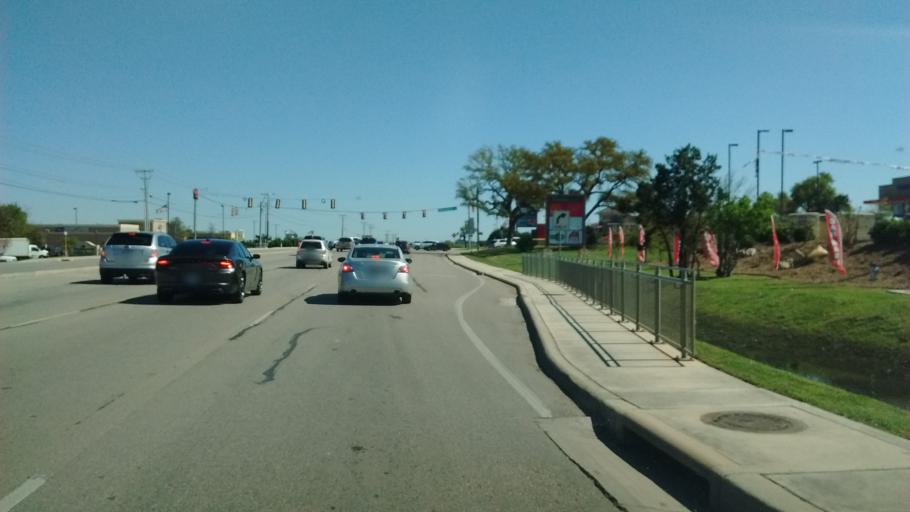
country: US
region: Texas
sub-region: Comal County
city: New Braunfels
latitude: 29.7180
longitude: -98.1619
